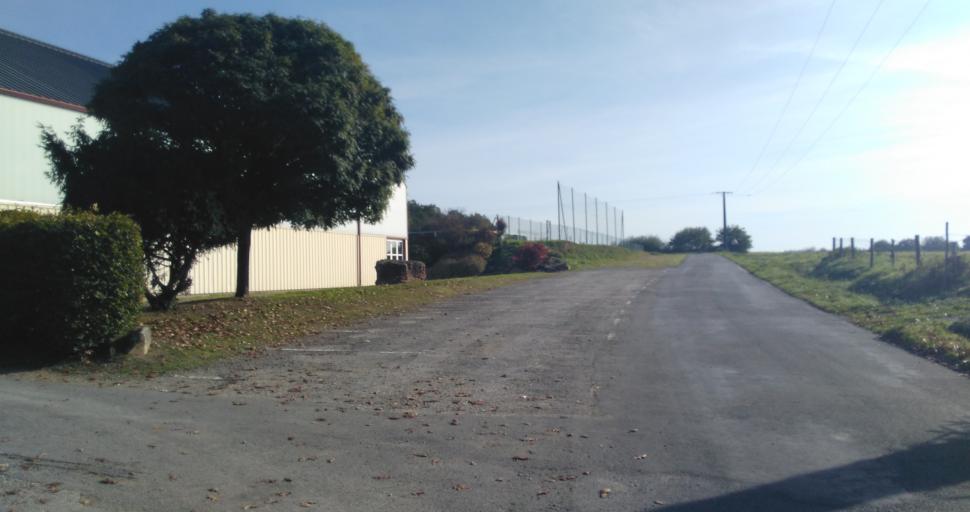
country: FR
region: Brittany
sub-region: Departement du Morbihan
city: Peillac
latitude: 47.7435
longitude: -2.2092
